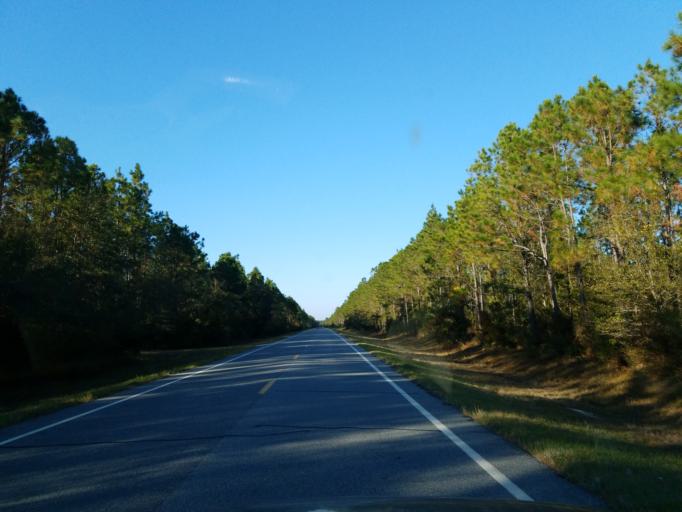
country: US
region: Georgia
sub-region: Echols County
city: Statenville
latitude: 30.8708
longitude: -83.0522
